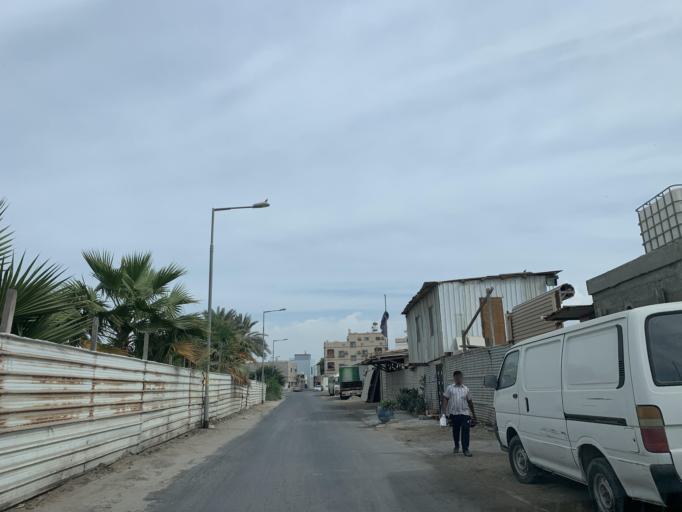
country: BH
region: Central Governorate
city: Madinat Hamad
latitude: 26.1144
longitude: 50.4786
